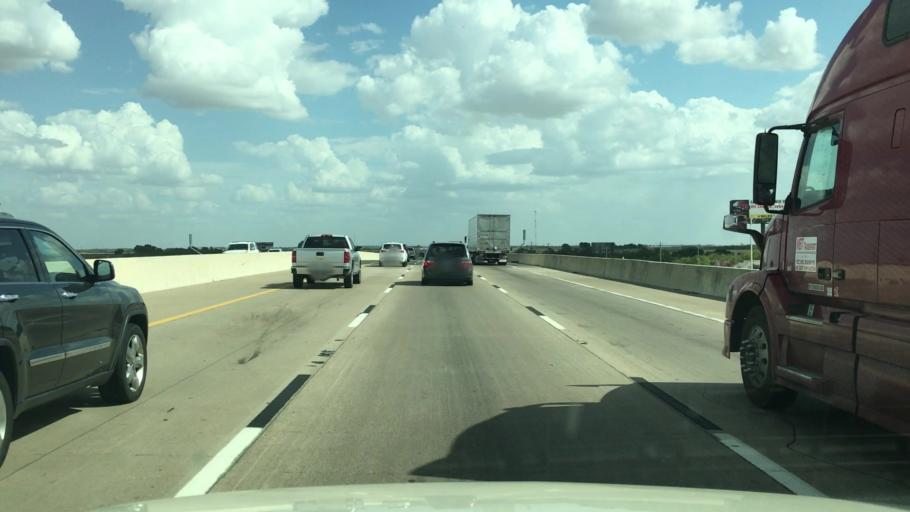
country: US
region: Texas
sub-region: Hill County
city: Hillsboro
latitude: 31.9579
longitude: -97.1159
